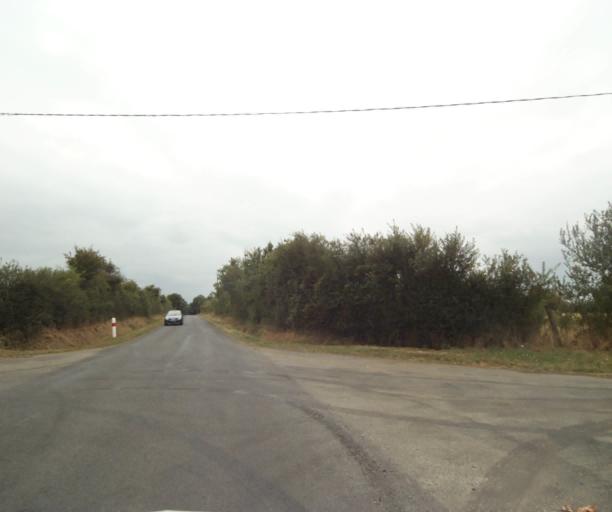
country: FR
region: Pays de la Loire
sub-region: Departement de la Sarthe
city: Solesmes
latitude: 47.8303
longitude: -0.2840
